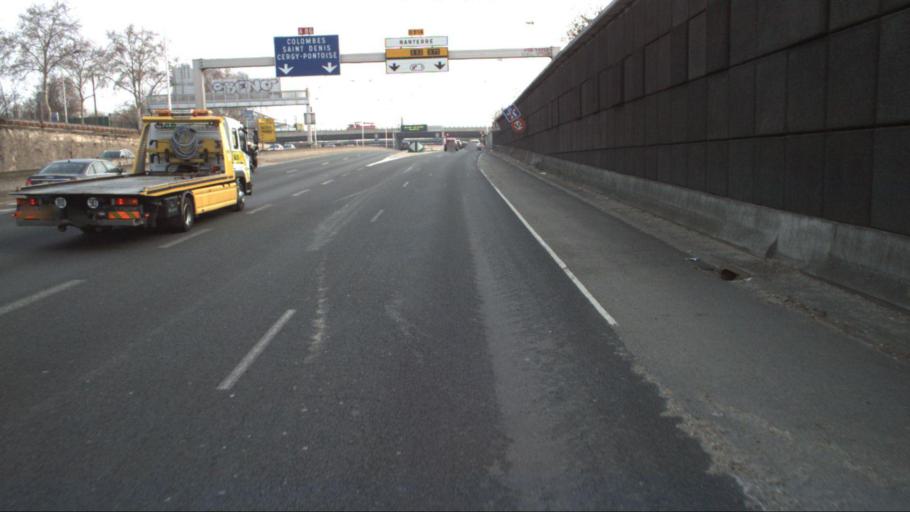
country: FR
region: Ile-de-France
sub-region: Departement des Hauts-de-Seine
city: Nanterre
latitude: 48.9055
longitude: 2.2097
